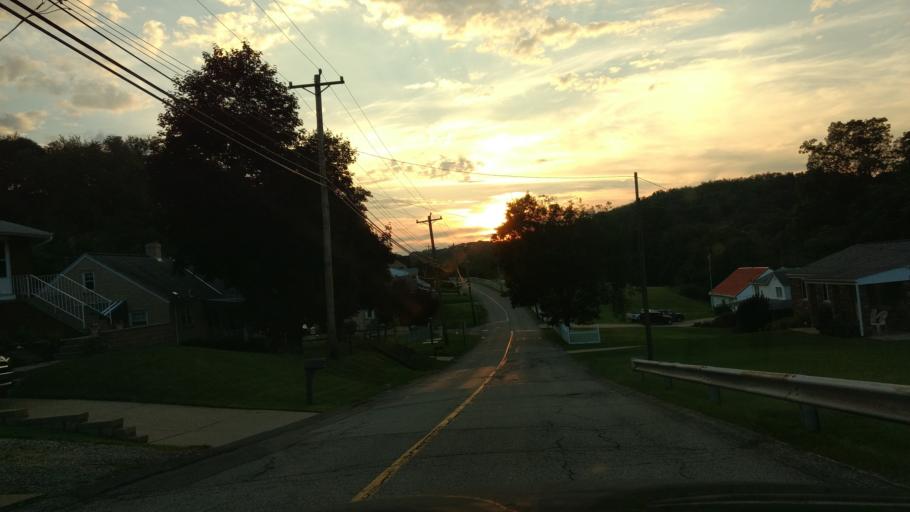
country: US
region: Pennsylvania
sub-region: Allegheny County
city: Bellevue
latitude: 40.4996
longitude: -80.0306
